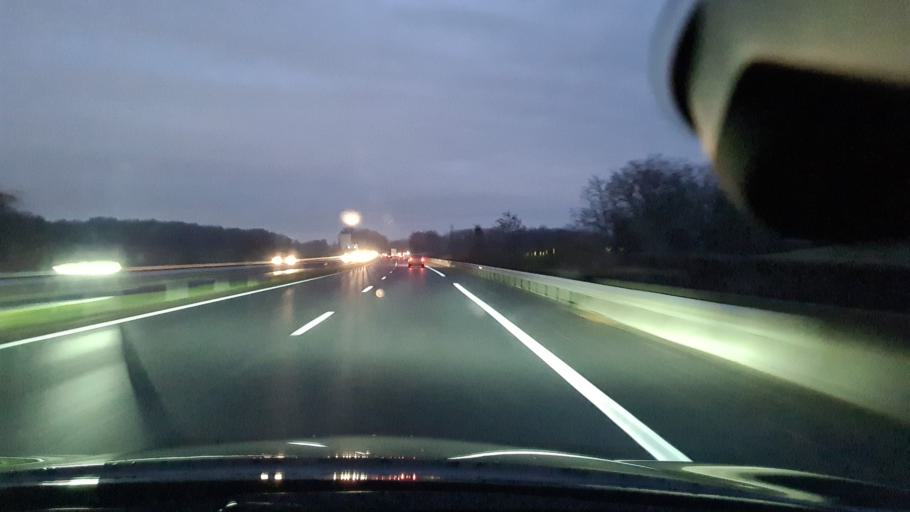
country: FR
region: Rhone-Alpes
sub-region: Departement du Rhone
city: Meyzieu
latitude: 45.7496
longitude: 5.0050
